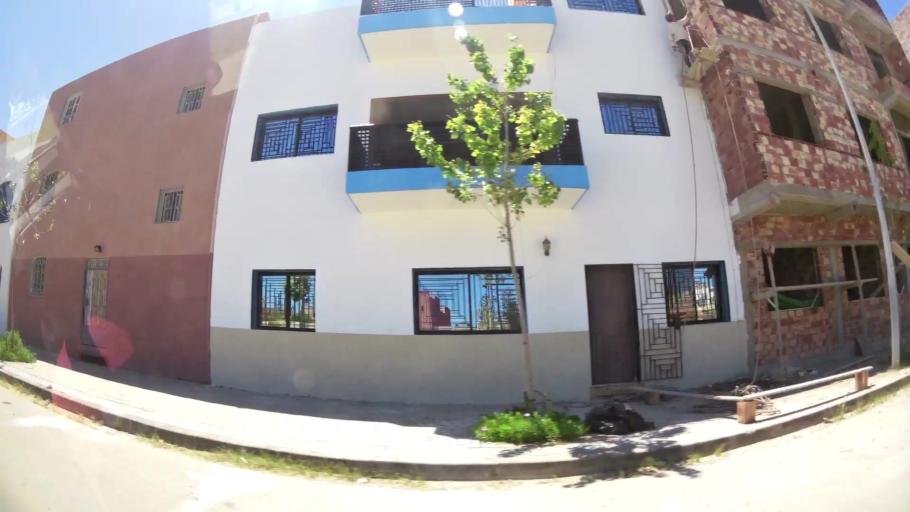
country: MA
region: Oriental
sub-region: Berkane-Taourirt
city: Madagh
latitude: 35.0848
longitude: -2.2305
